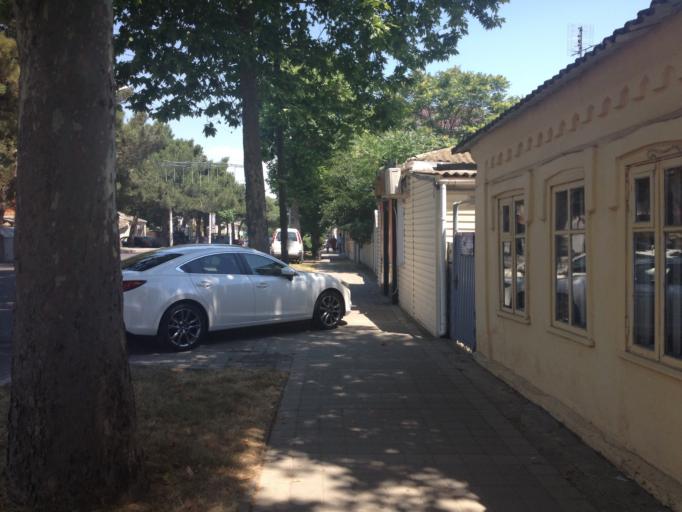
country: RU
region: Krasnodarskiy
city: Anapa
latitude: 44.8915
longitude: 37.3118
